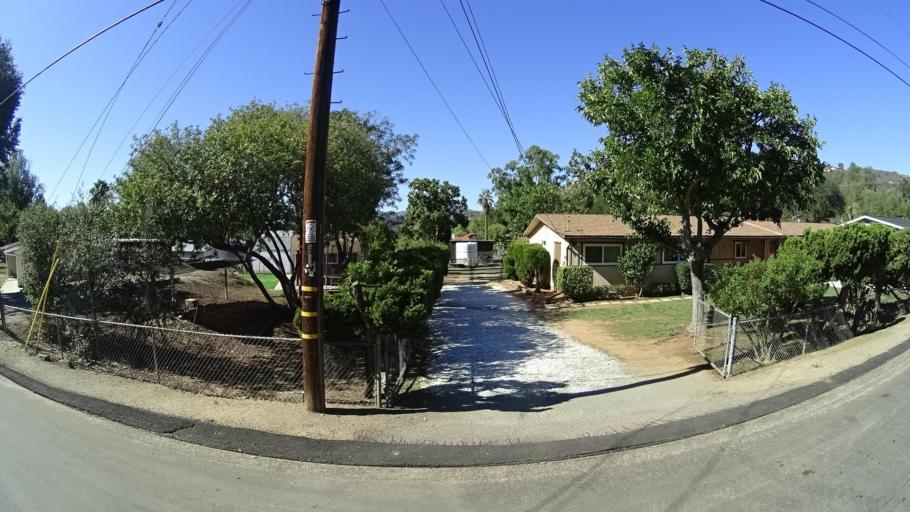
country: US
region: California
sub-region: San Diego County
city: Jamul
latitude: 32.7245
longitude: -116.8725
